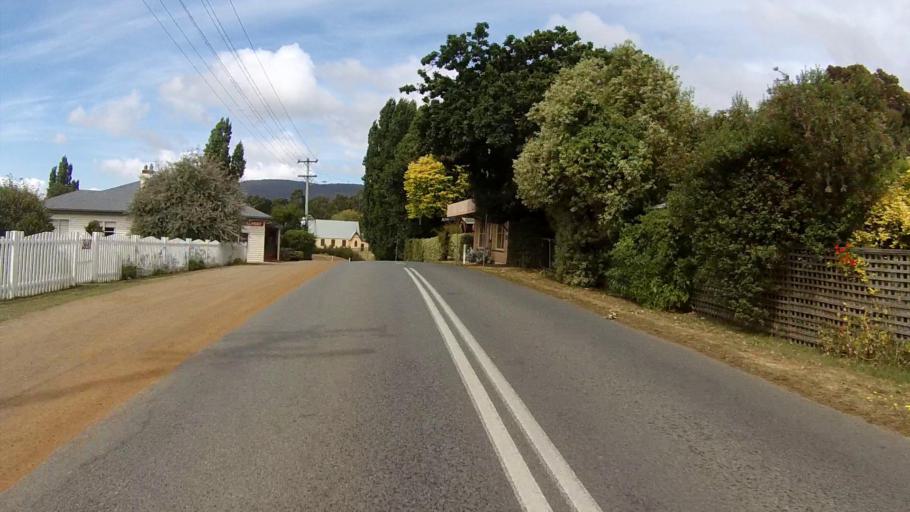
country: AU
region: Tasmania
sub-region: Kingborough
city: Kettering
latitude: -43.1601
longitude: 147.2387
